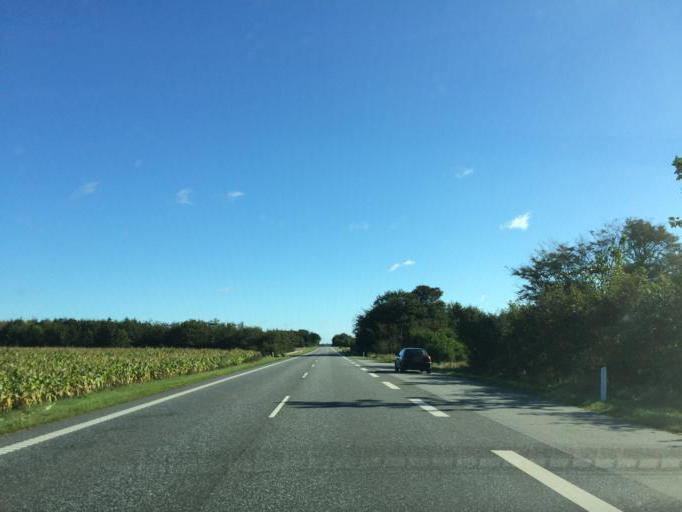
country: DK
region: Central Jutland
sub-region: Skive Kommune
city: Skive
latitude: 56.4035
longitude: 8.9718
